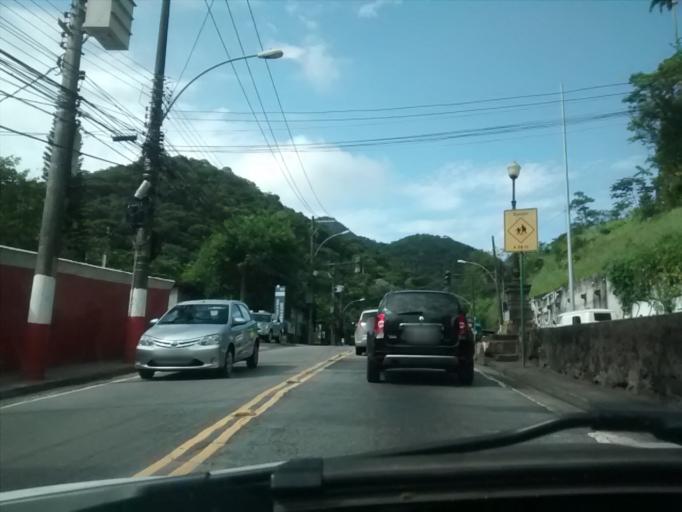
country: BR
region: Rio de Janeiro
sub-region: Rio De Janeiro
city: Rio de Janeiro
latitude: -22.9663
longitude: -43.2776
